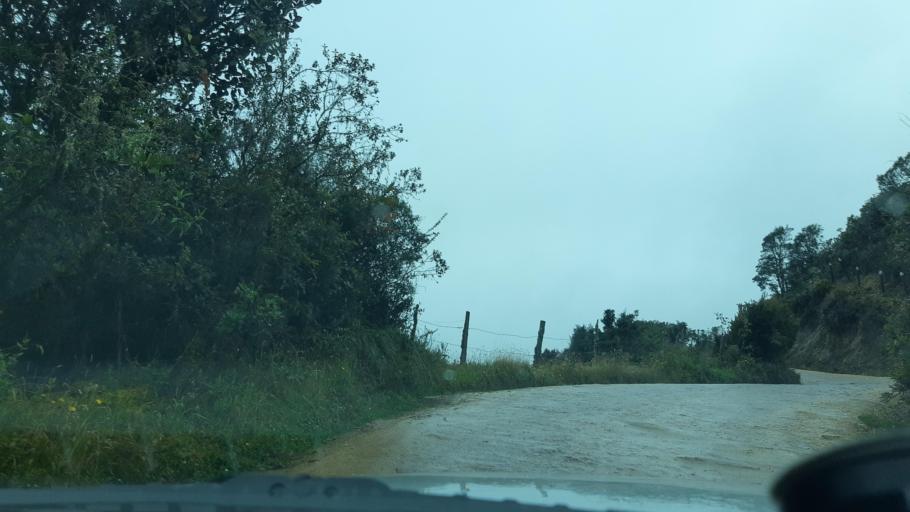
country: CO
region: Cundinamarca
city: Umbita
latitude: 5.2163
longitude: -73.5228
